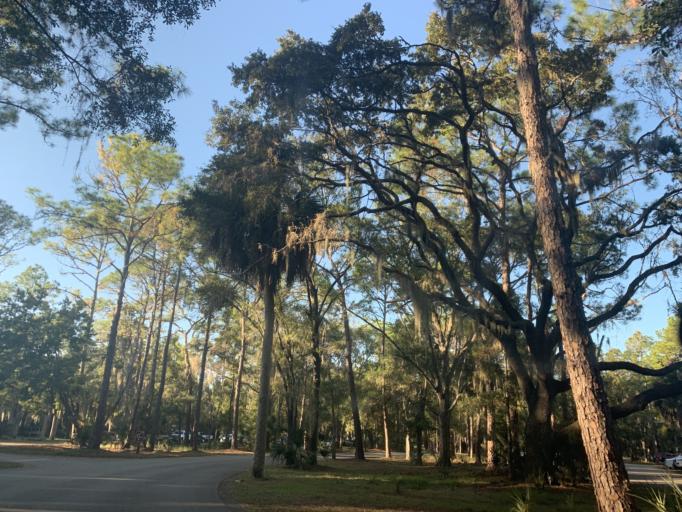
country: US
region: Florida
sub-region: Pinellas County
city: East Lake
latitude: 28.0943
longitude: -82.7089
